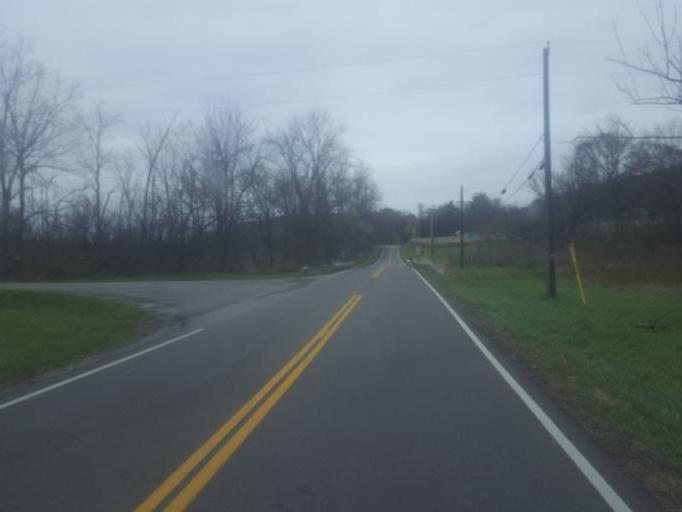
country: US
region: Ohio
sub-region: Ashland County
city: Loudonville
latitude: 40.7306
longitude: -82.2887
